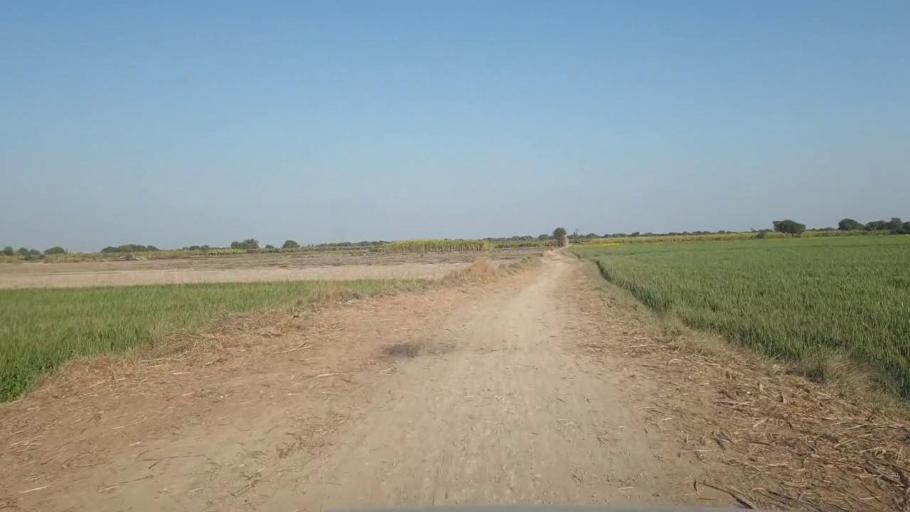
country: PK
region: Sindh
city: Chambar
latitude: 25.2881
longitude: 68.8708
